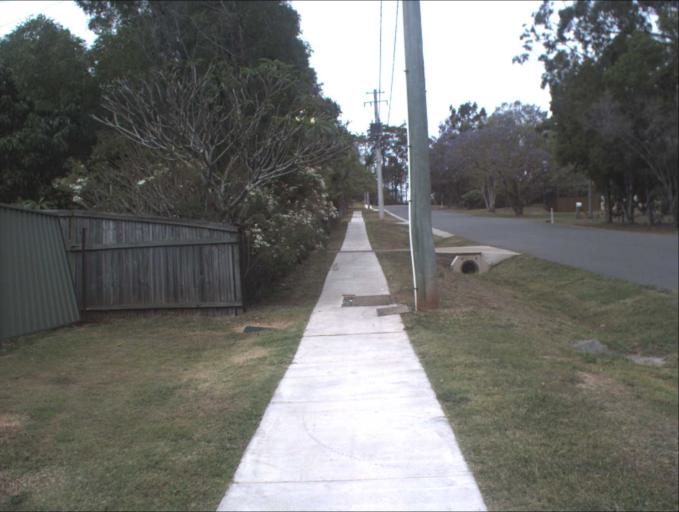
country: AU
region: Queensland
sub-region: Logan
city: Slacks Creek
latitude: -27.6615
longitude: 153.1644
